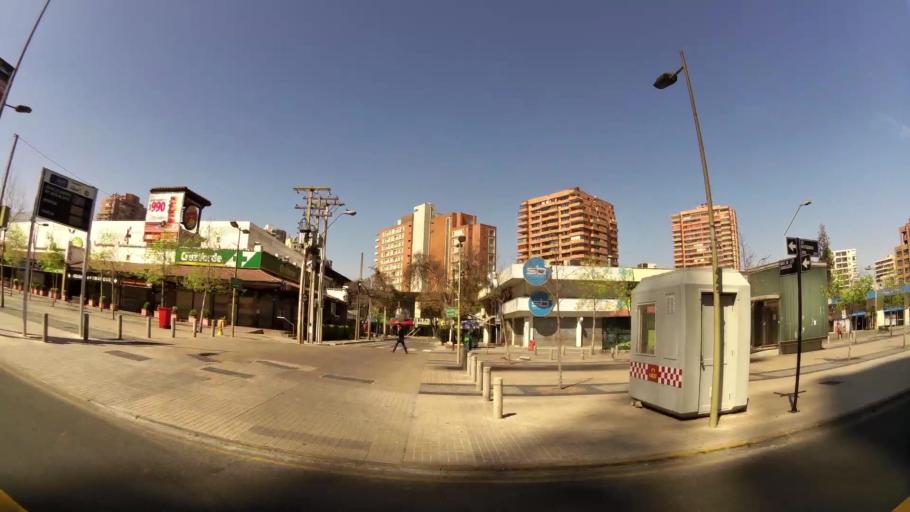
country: CL
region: Santiago Metropolitan
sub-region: Provincia de Santiago
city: Villa Presidente Frei, Nunoa, Santiago, Chile
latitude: -33.4093
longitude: -70.5689
